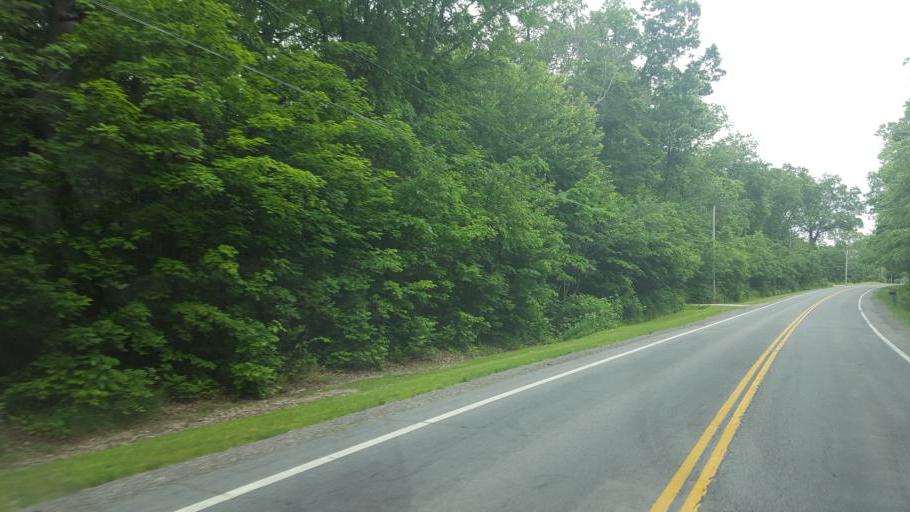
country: US
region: Ohio
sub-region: Crawford County
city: Galion
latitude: 40.7656
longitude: -82.8795
